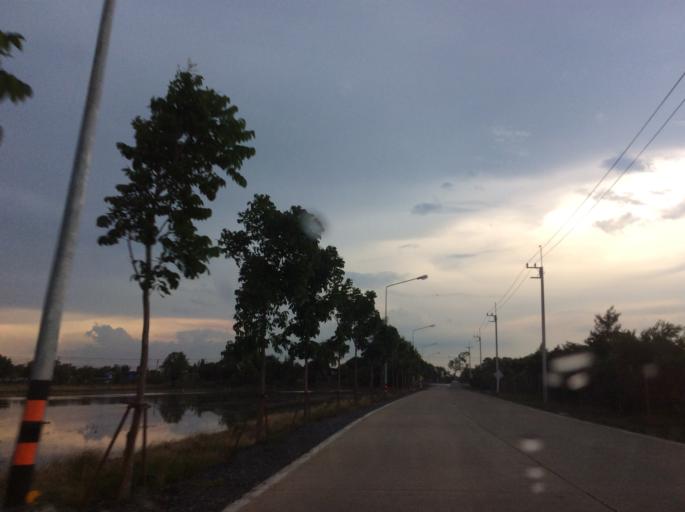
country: TH
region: Pathum Thani
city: Thanyaburi
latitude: 14.0030
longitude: 100.7328
